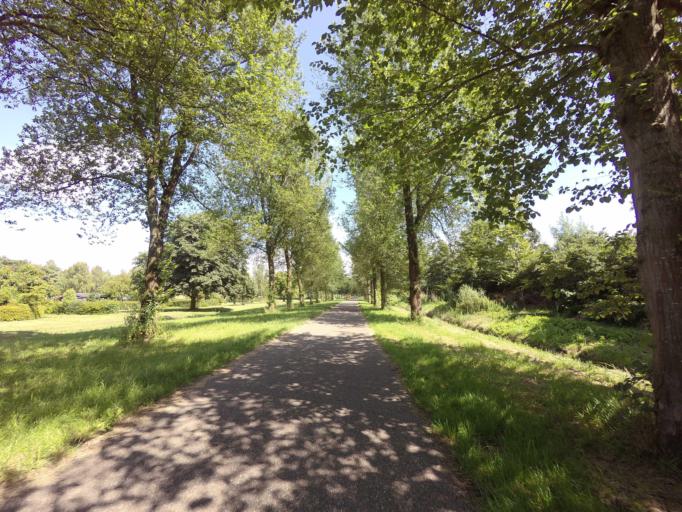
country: NL
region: North Holland
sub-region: Gemeente Huizen
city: Huizen
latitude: 52.3347
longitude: 5.2456
